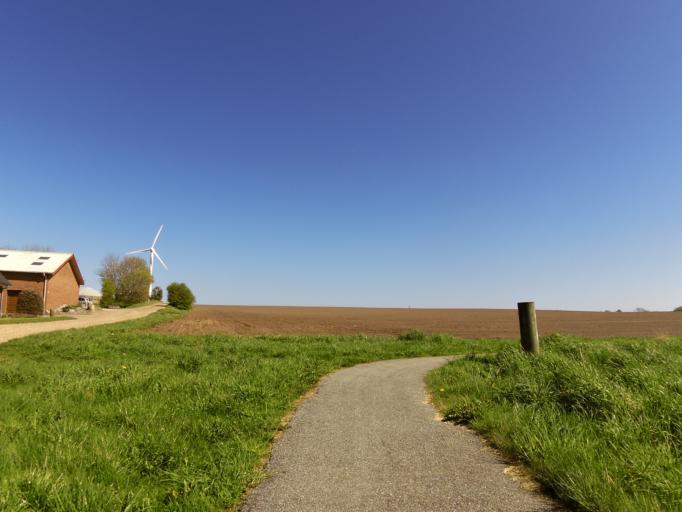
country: DK
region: Central Jutland
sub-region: Holstebro Kommune
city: Vinderup
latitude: 56.6007
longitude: 8.7737
